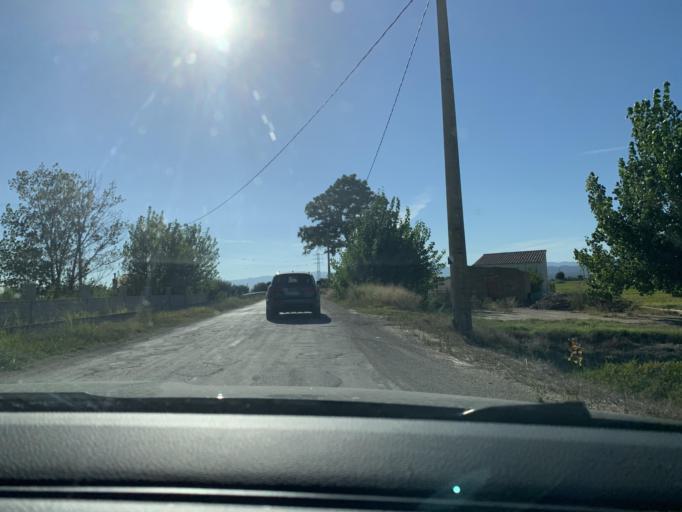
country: ES
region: Catalonia
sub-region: Provincia de Tarragona
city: Deltebre
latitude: 40.7480
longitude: 0.7300
